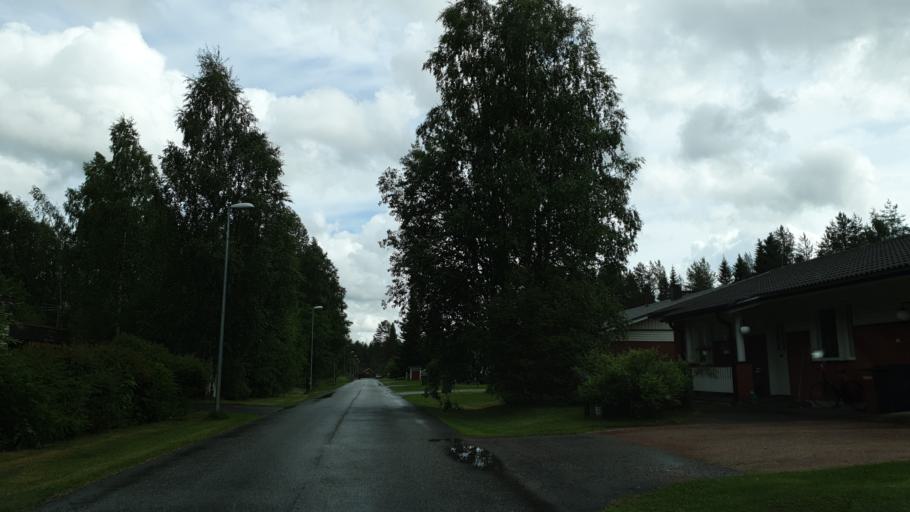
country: FI
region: Kainuu
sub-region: Kehys-Kainuu
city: Kuhmo
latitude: 64.1184
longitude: 29.5083
